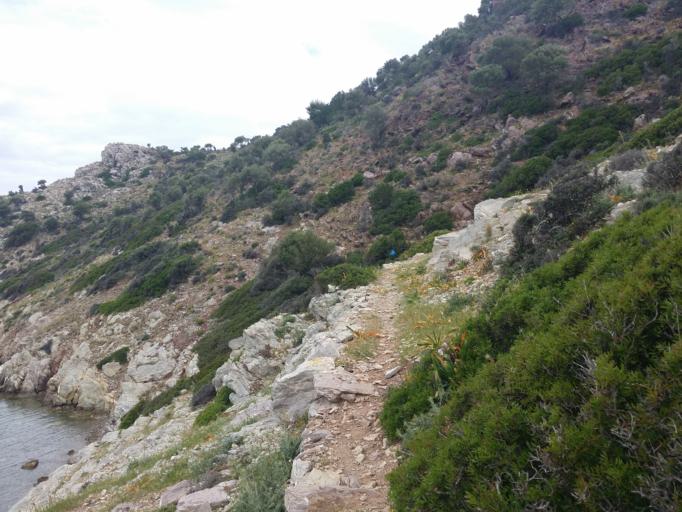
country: GR
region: Attica
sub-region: Nomos Piraios
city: Galatas
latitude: 37.5244
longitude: 23.4271
